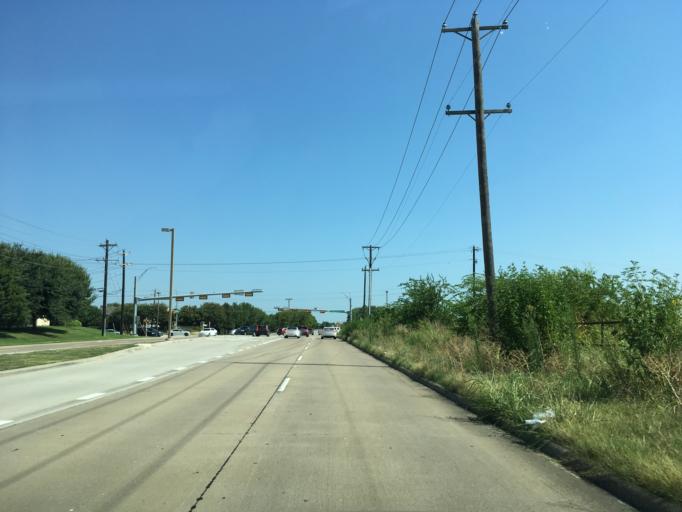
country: US
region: Texas
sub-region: Collin County
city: Fairview
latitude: 33.1580
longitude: -96.6805
